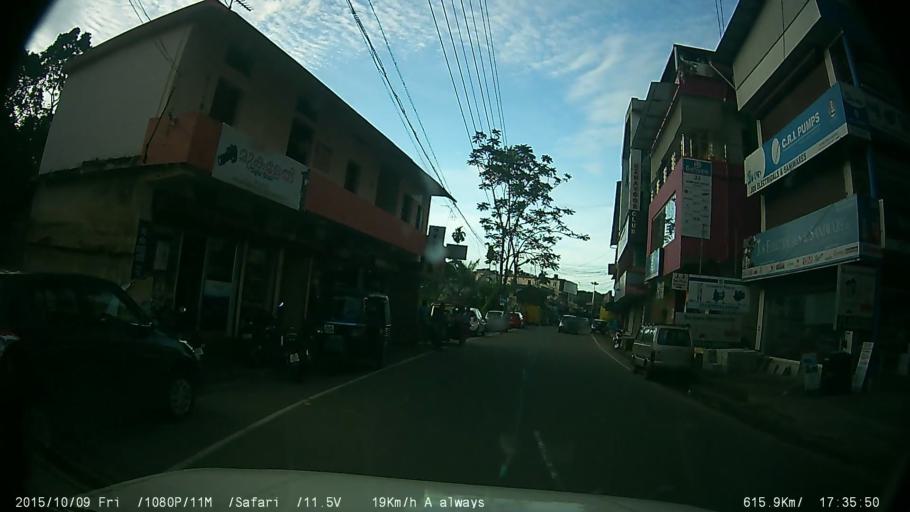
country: IN
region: Kerala
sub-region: Kottayam
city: Palackattumala
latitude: 9.7876
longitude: 76.6102
